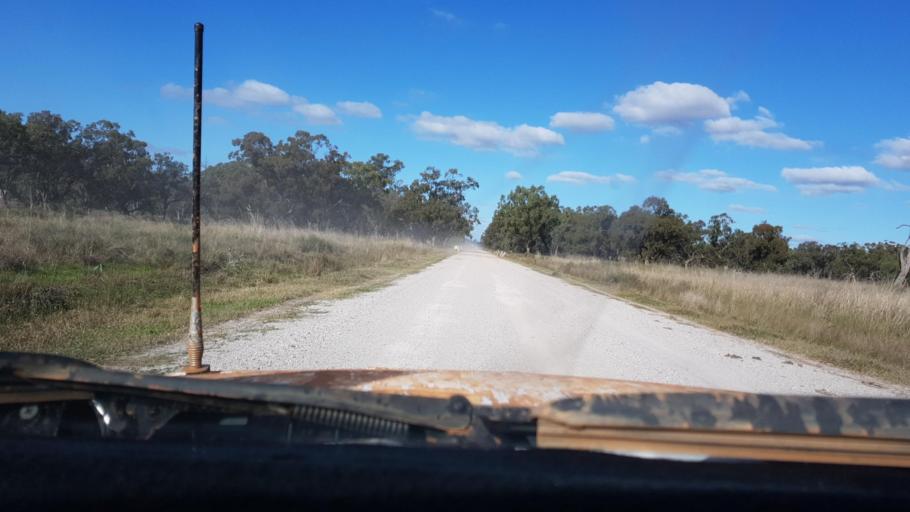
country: AU
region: New South Wales
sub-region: Lachlan
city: Condobolin
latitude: -33.1275
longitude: 147.2565
